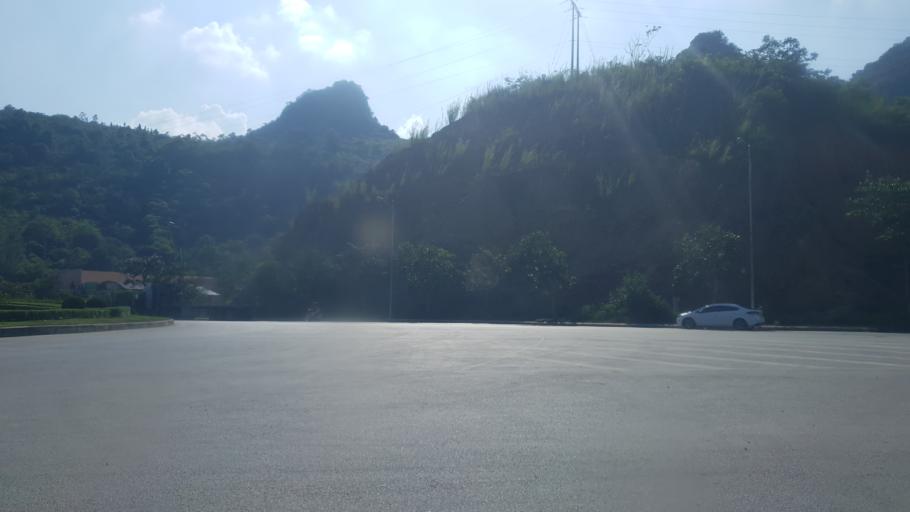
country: VN
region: Lang Son
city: Thi Tran Cao Loc
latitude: 21.9595
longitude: 106.7059
